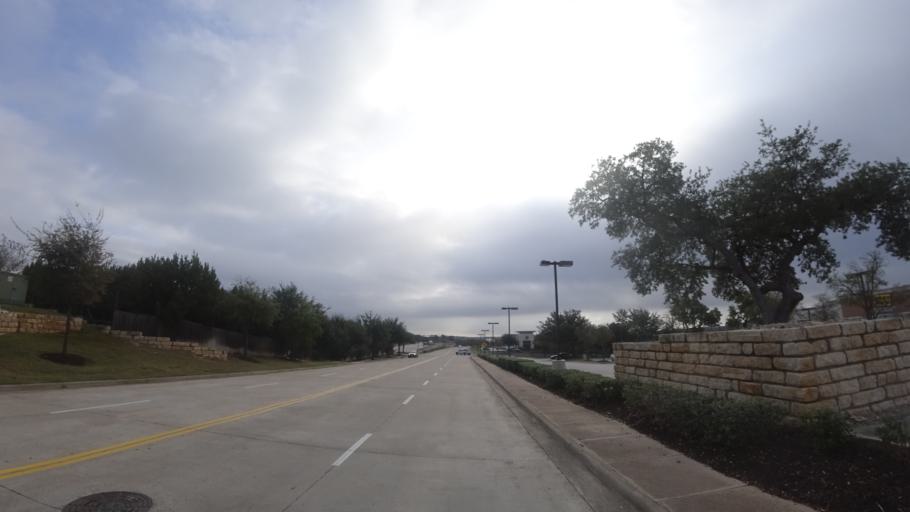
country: US
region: Texas
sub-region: Travis County
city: Bee Cave
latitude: 30.3064
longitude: -97.9442
